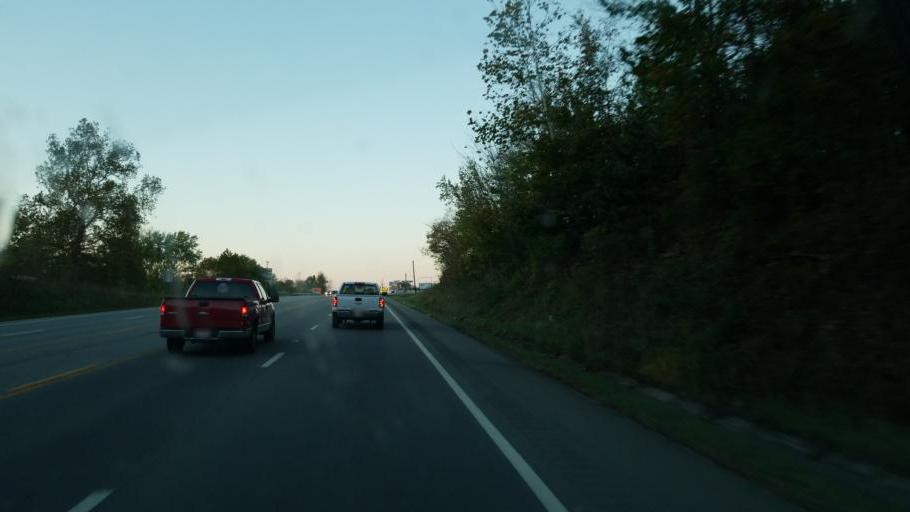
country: US
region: Ohio
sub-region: Pike County
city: Waverly
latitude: 39.1426
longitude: -82.9775
